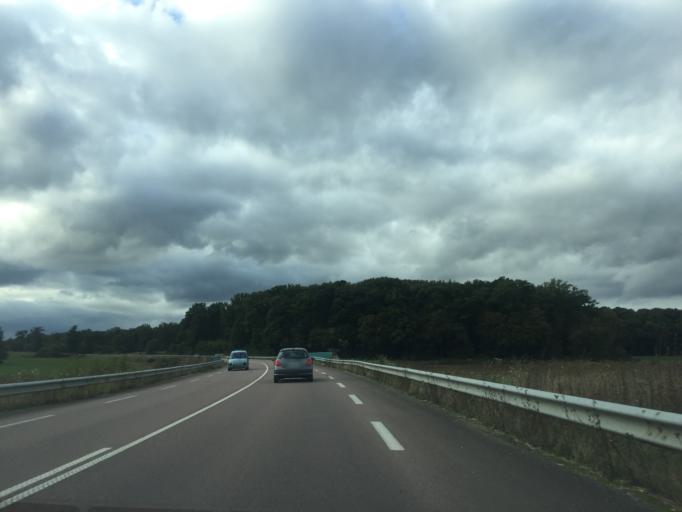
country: FR
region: Lorraine
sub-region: Departement des Vosges
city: Chatenois
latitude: 48.2982
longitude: 5.8822
